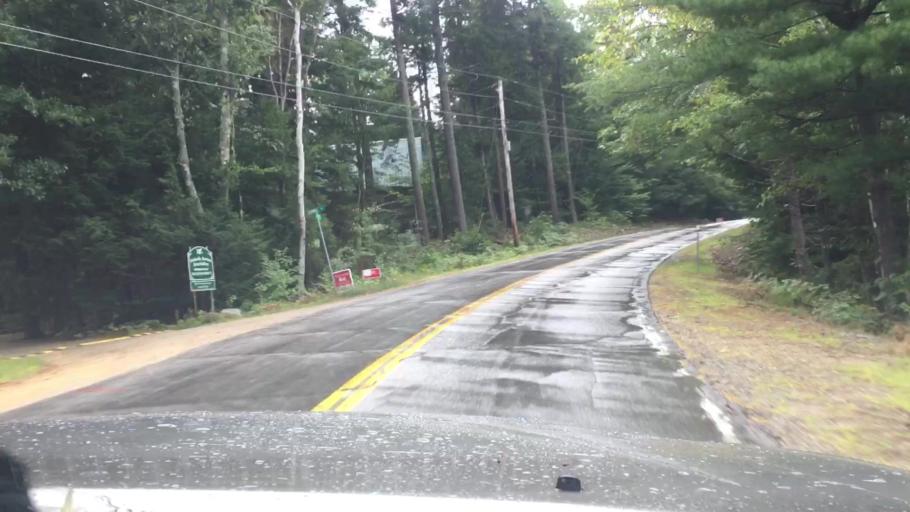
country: US
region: New Hampshire
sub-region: Belknap County
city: Meredith
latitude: 43.6636
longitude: -71.5452
